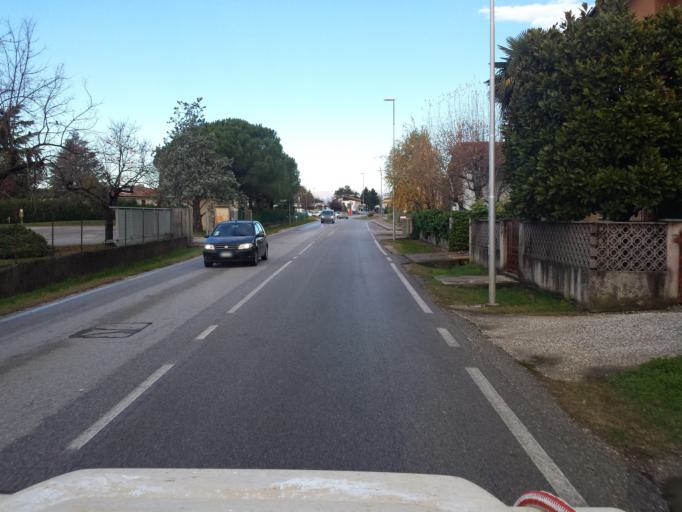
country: IT
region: Friuli Venezia Giulia
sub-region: Provincia di Udine
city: San Giovanni al Natisone
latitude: 45.9687
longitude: 13.3981
